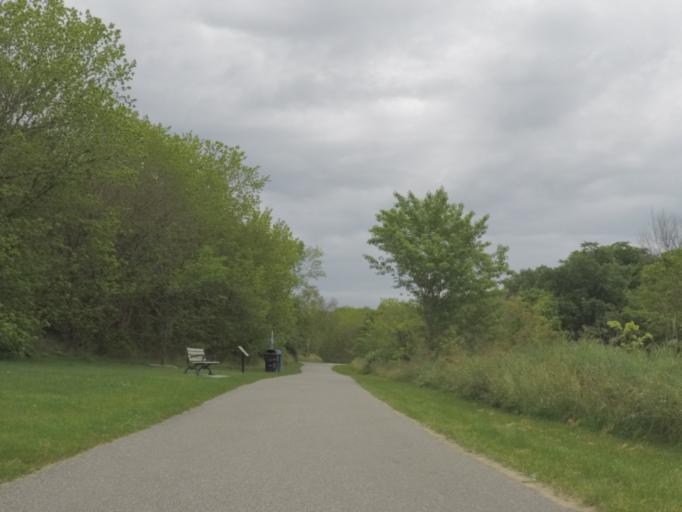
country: CA
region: Ontario
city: Etobicoke
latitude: 43.6632
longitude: -79.5647
